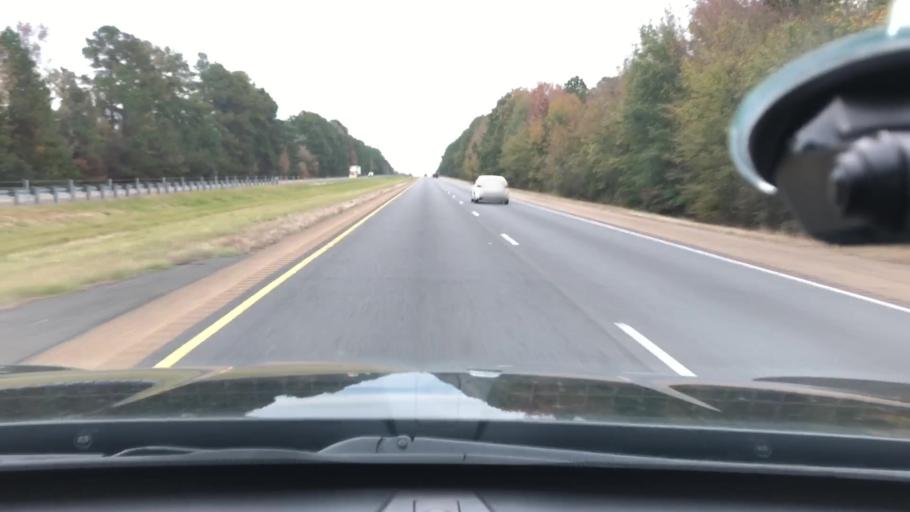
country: US
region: Arkansas
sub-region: Clark County
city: Gurdon
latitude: 33.9720
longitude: -93.2083
